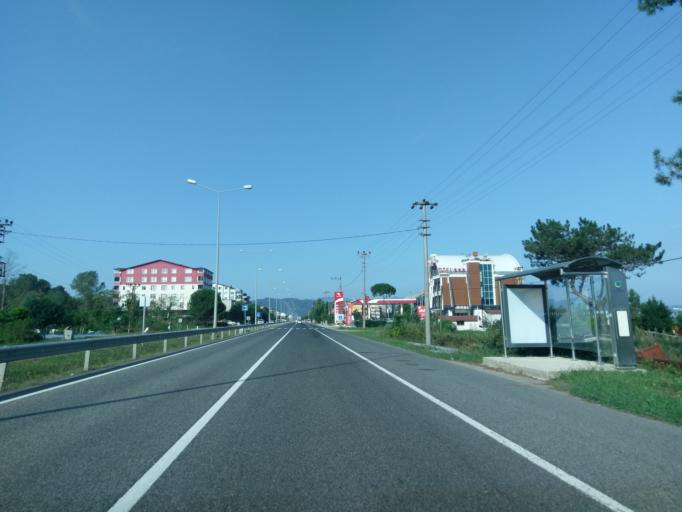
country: TR
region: Ordu
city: Bolaman
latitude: 41.0267
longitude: 37.5659
